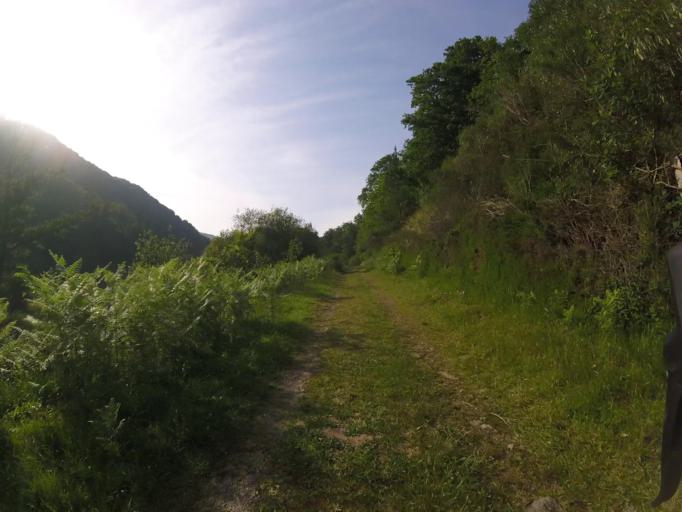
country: ES
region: Navarre
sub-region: Provincia de Navarra
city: Arano
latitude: 43.2333
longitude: -1.8684
